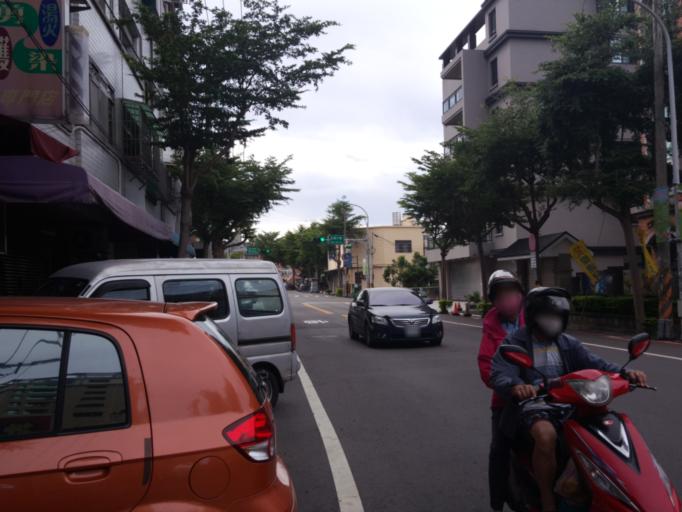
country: TW
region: Taiwan
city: Taoyuan City
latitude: 25.0549
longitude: 121.2943
